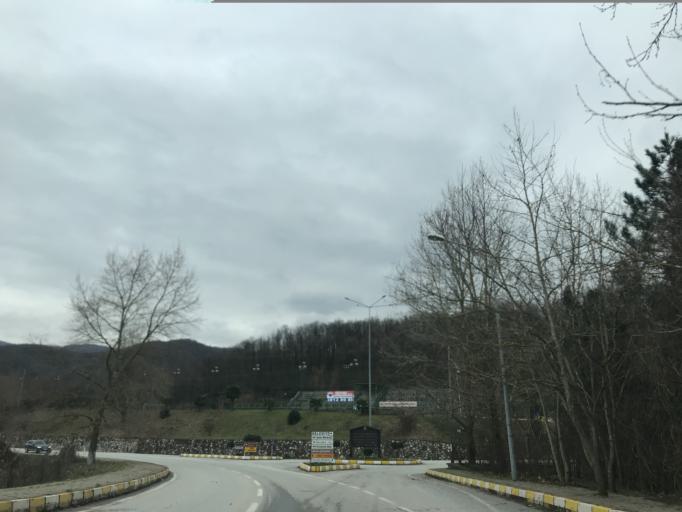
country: TR
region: Yalova
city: Termal
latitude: 40.6058
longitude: 29.1834
